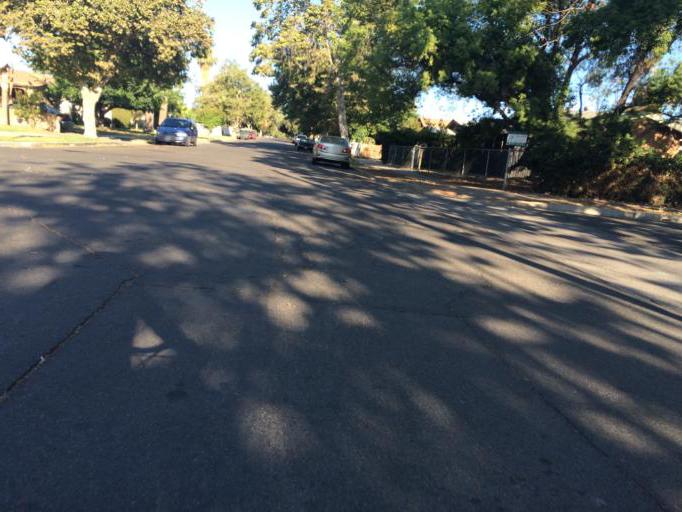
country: US
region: California
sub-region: Fresno County
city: Fresno
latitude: 36.7496
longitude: -119.7608
